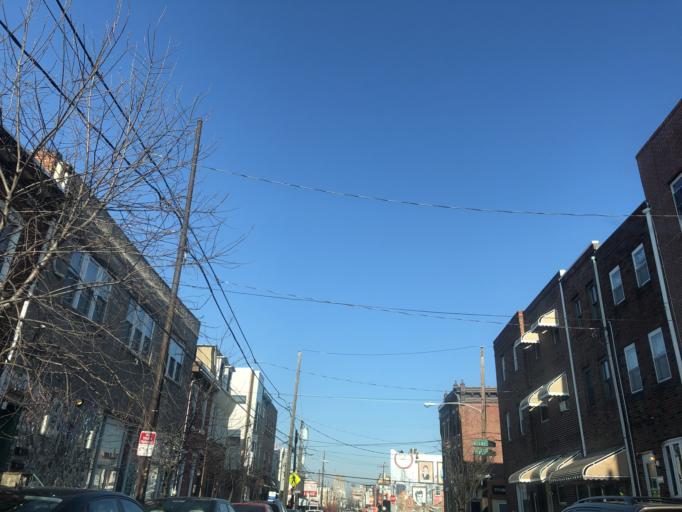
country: US
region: Pennsylvania
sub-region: Philadelphia County
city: Philadelphia
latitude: 39.9324
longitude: -75.1593
